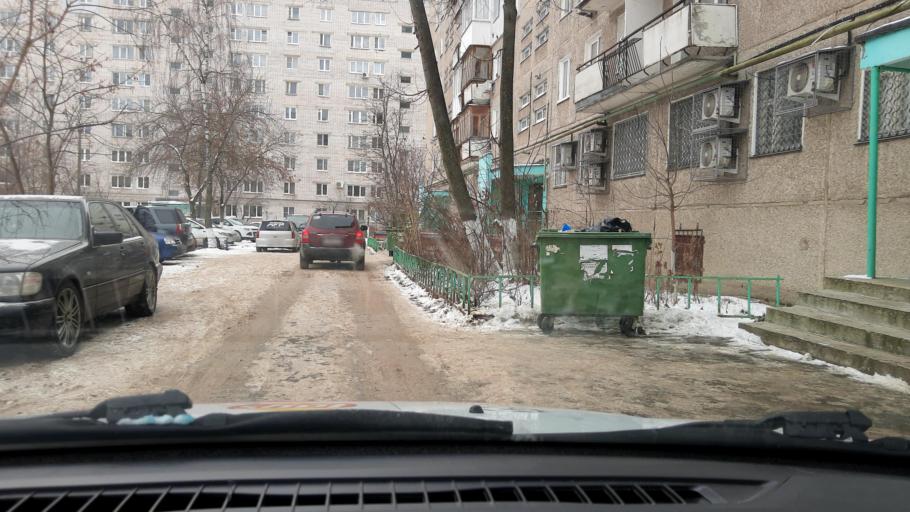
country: RU
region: Nizjnij Novgorod
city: Dzerzhinsk
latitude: 56.2284
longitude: 43.4046
